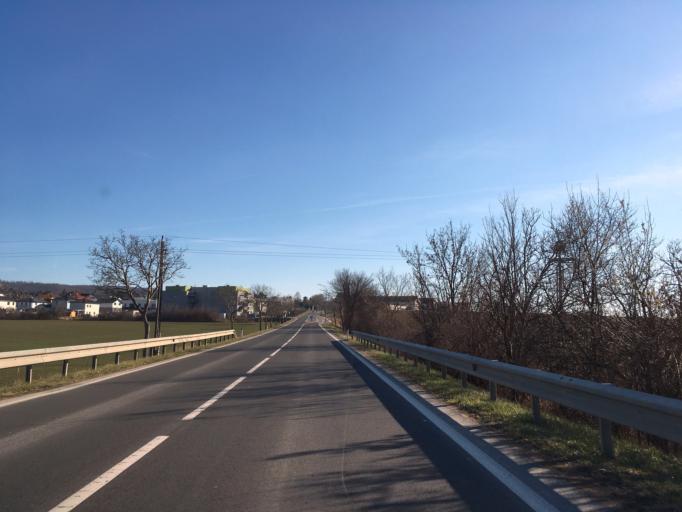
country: AT
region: Burgenland
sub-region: Eisenstadt-Umgebung
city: Hornstein
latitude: 47.8904
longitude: 16.4383
